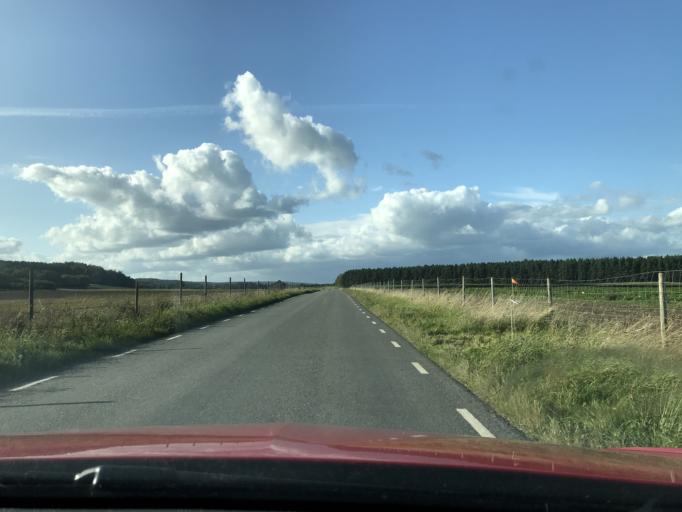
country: SE
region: Skane
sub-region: Kristianstads Kommun
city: Degeberga
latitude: 55.8524
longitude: 14.0770
